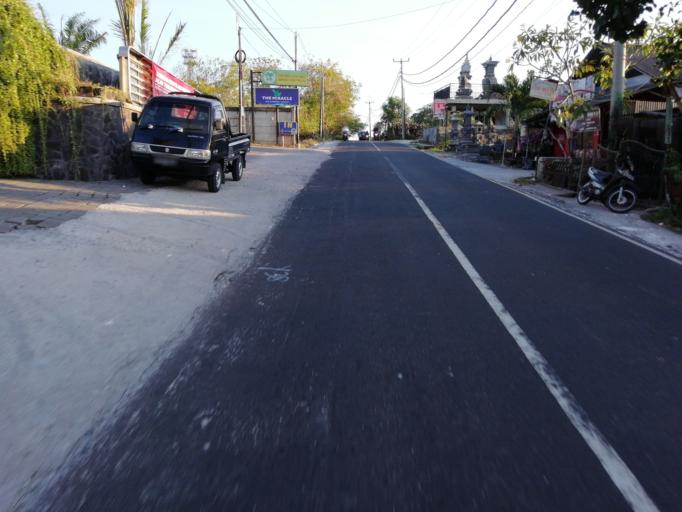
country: ID
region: Bali
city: Bualu
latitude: -8.8168
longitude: 115.1908
